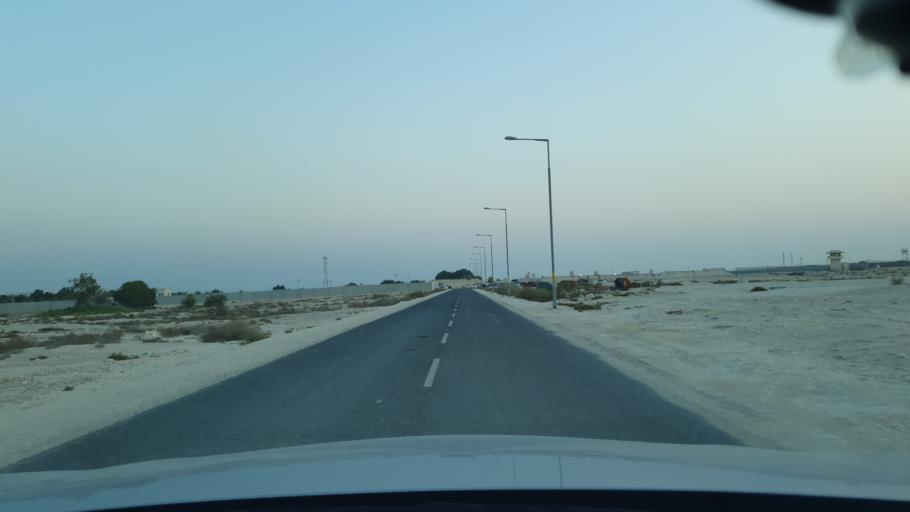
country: BH
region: Central Governorate
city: Dar Kulayb
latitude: 25.9583
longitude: 50.6113
